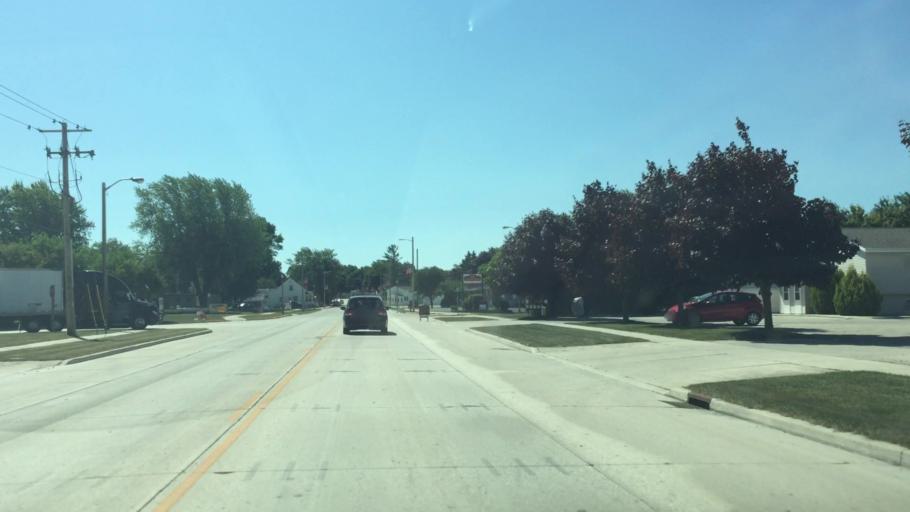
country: US
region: Wisconsin
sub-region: Calumet County
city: New Holstein
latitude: 43.9532
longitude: -88.1032
